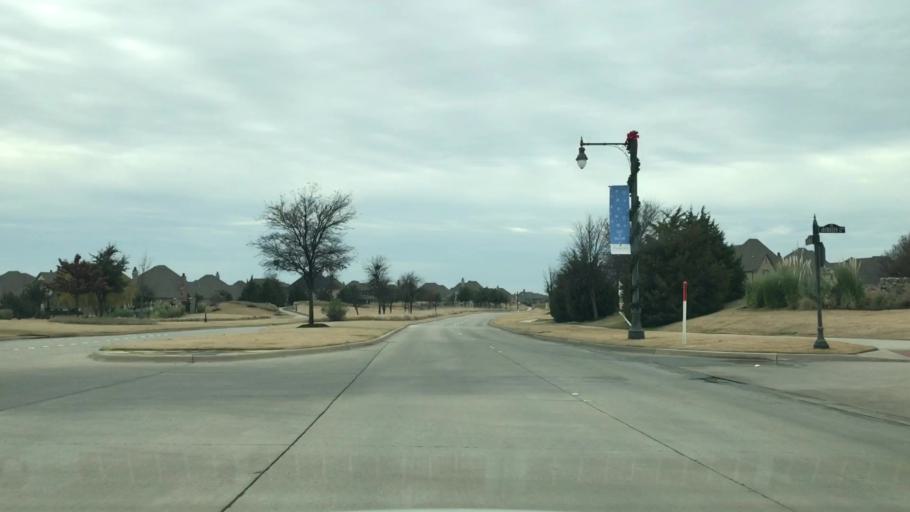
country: US
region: Texas
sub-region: Denton County
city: The Colony
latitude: 33.1110
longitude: -96.9184
